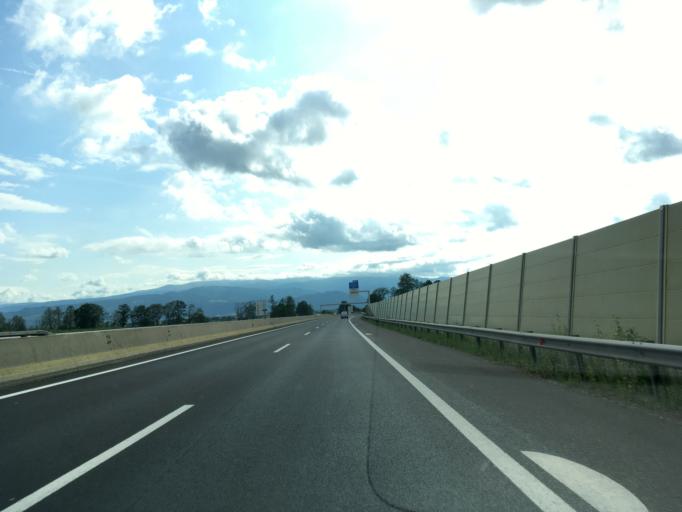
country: AT
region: Styria
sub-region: Politischer Bezirk Murtal
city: Spielberg bei Knittelfeld
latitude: 47.2139
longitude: 14.7937
